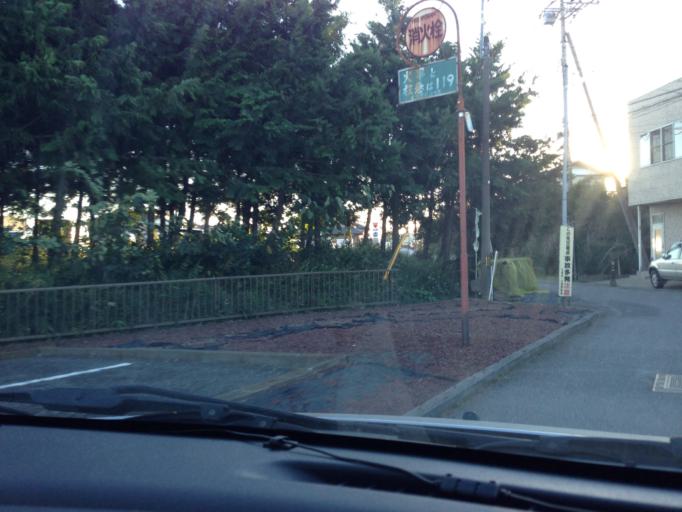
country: JP
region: Ibaraki
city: Naka
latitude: 36.0407
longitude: 140.1579
